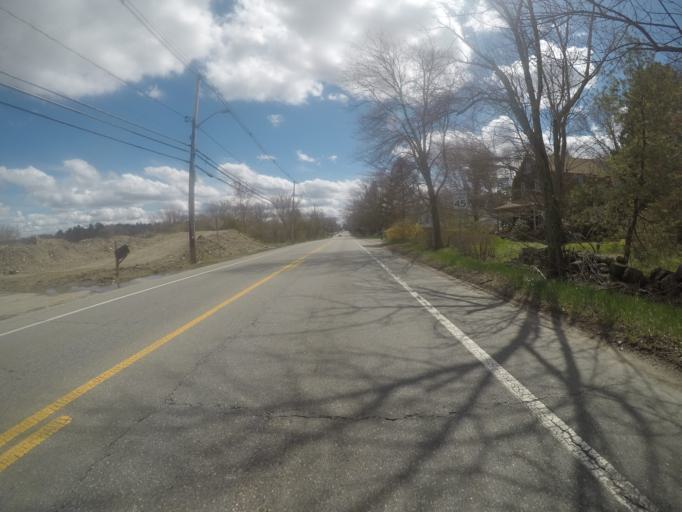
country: US
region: Massachusetts
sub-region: Plymouth County
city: West Bridgewater
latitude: 42.0216
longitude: -71.0664
